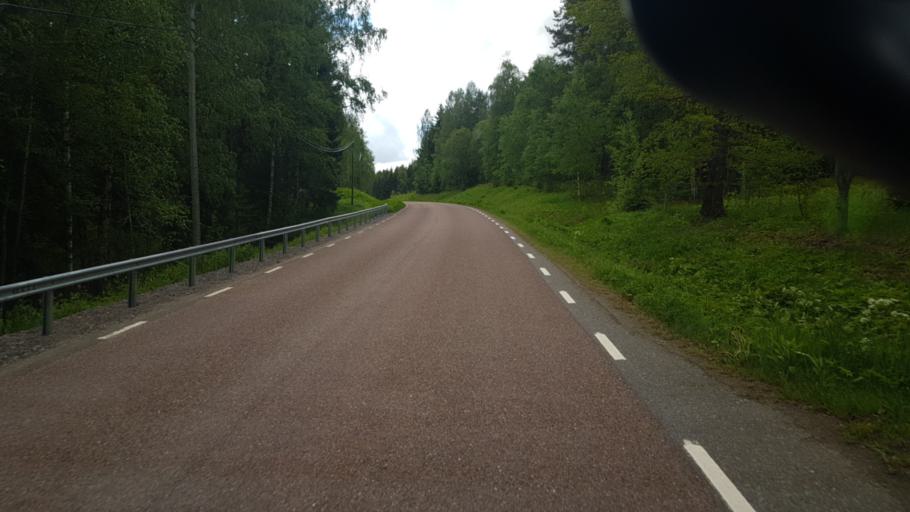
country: NO
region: Hedmark
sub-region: Eidskog
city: Skotterud
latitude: 59.7643
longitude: 12.0485
